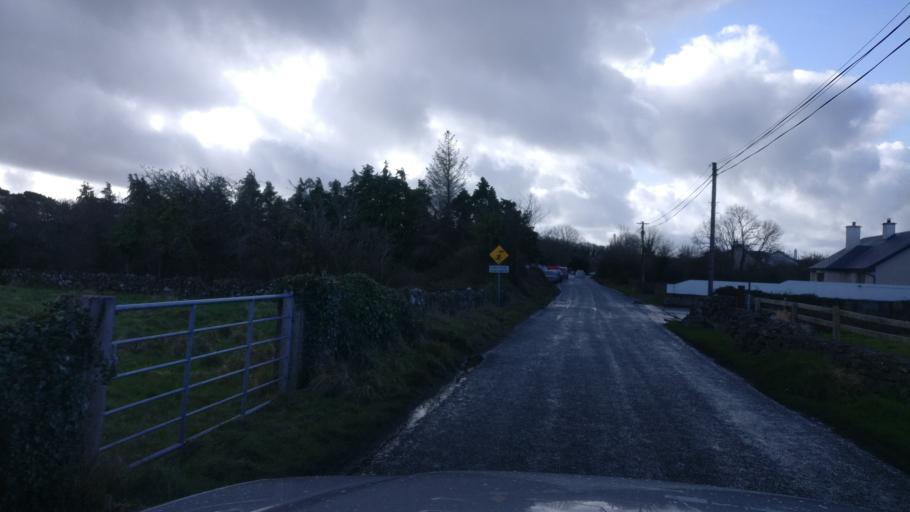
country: IE
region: Connaught
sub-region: County Galway
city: Oranmore
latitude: 53.2498
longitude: -8.9069
